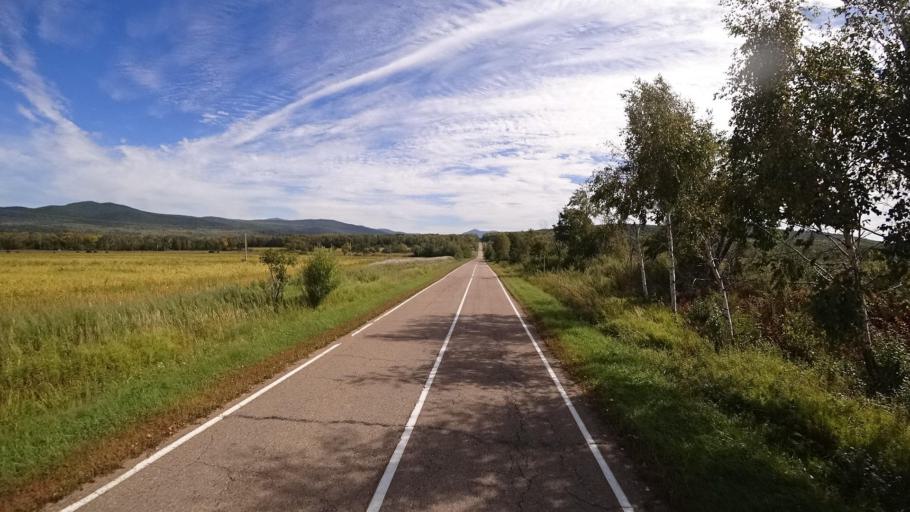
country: RU
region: Primorskiy
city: Yakovlevka
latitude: 44.4128
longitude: 133.5864
